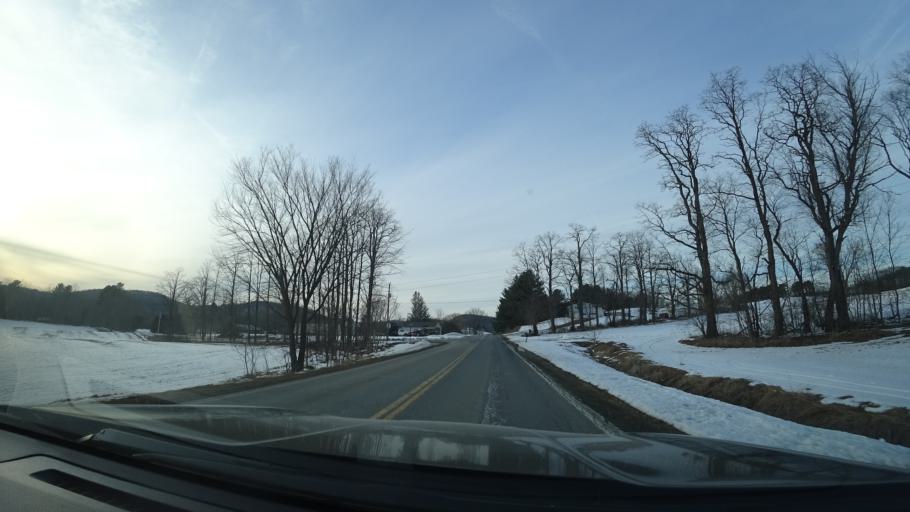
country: US
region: New York
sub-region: Washington County
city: Cambridge
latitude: 43.1696
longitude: -73.3511
